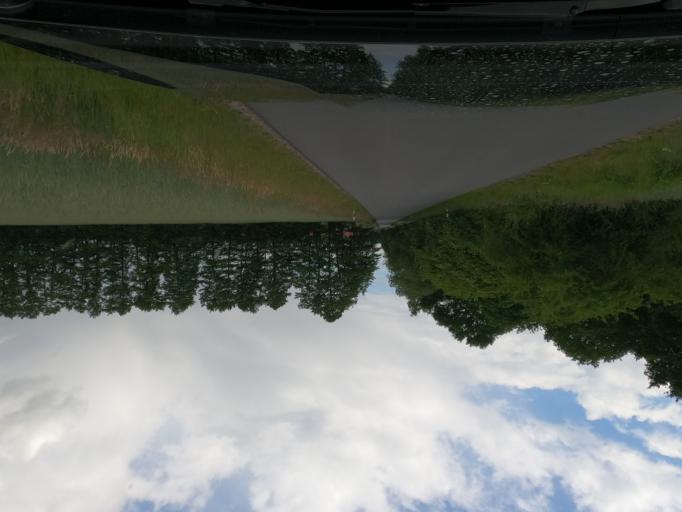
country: DE
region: Lower Saxony
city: Steimbke
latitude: 52.6427
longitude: 9.4493
